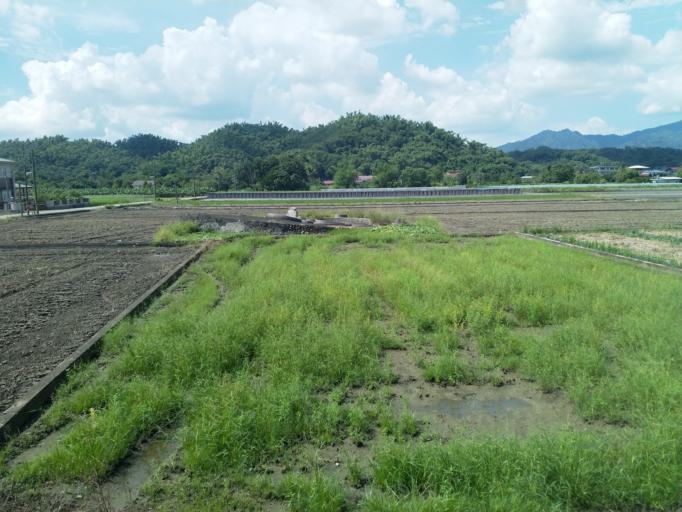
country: TW
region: Taiwan
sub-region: Pingtung
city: Pingtung
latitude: 22.8878
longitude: 120.5792
